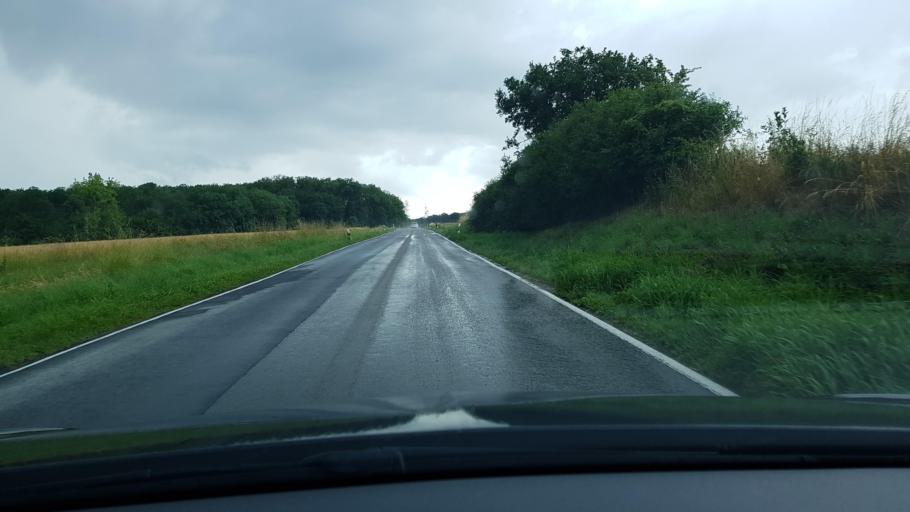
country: DE
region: Rheinland-Pfalz
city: Sinzig
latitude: 50.5161
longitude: 7.2379
